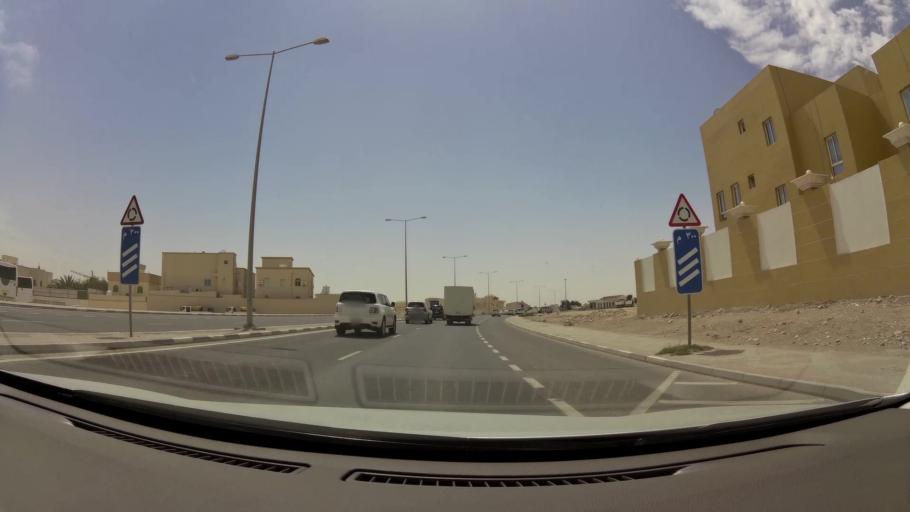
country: QA
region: Baladiyat ar Rayyan
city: Ar Rayyan
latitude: 25.2629
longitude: 51.4204
